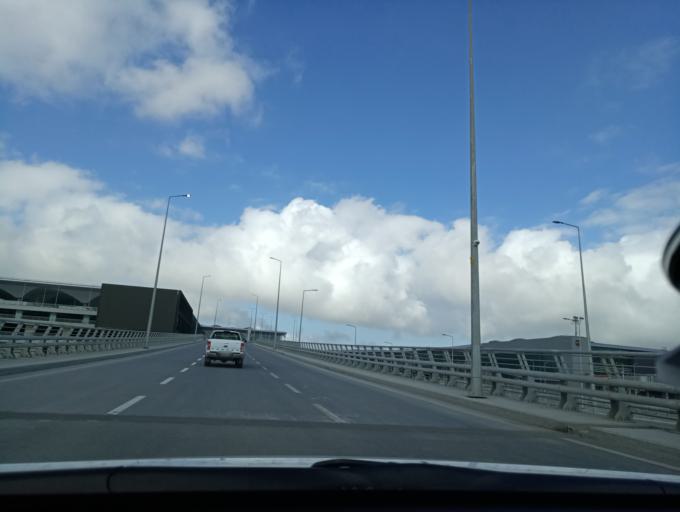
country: TR
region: Istanbul
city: Durusu
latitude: 41.2559
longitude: 28.7466
